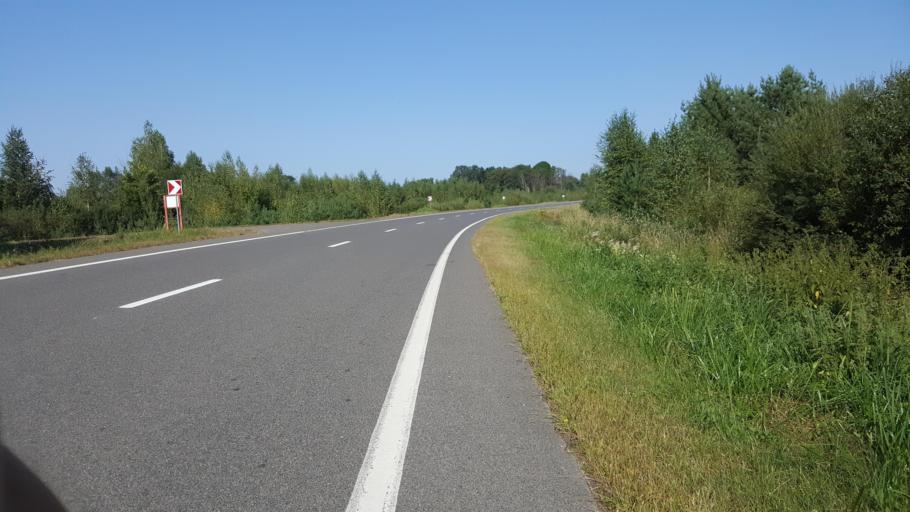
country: PL
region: Podlasie
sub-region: Powiat hajnowski
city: Hajnowka
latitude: 52.5628
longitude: 23.6072
